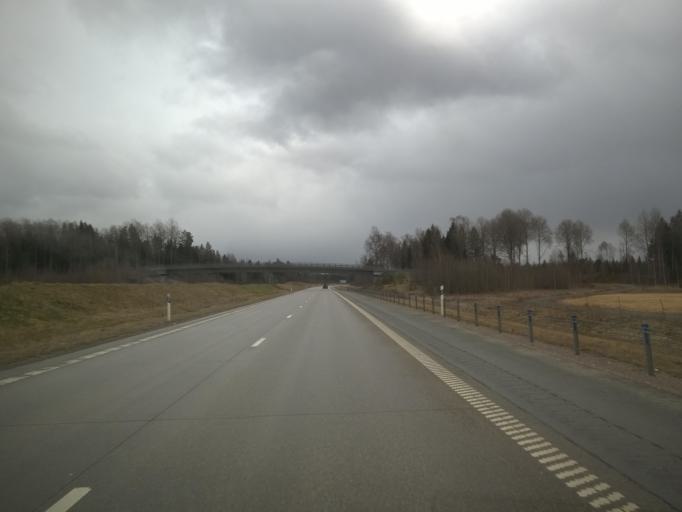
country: SE
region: Uppsala
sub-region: Uppsala Kommun
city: Storvreta
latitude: 60.0024
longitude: 17.6304
